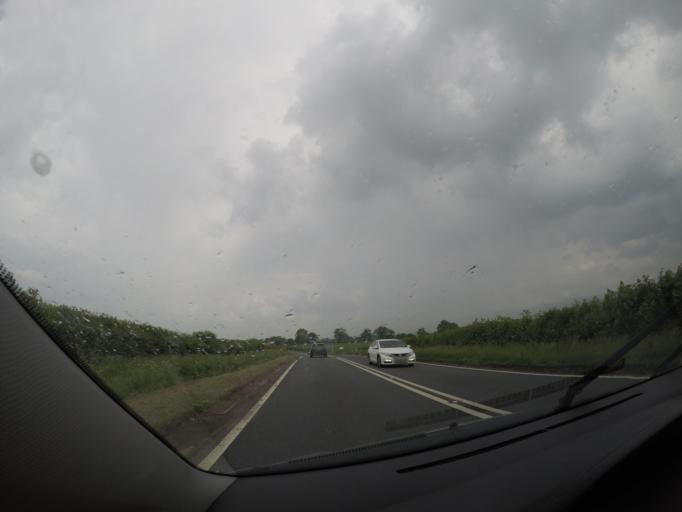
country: GB
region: England
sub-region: Cumbria
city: Appleby-in-Westmorland
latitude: 54.6047
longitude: -2.5391
